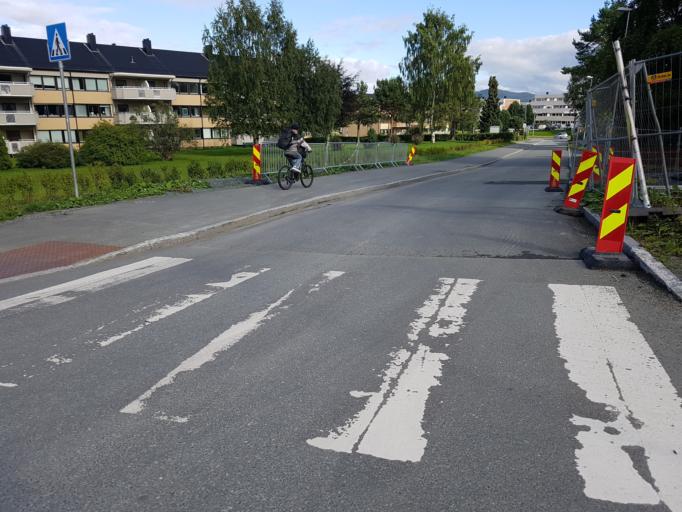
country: NO
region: Sor-Trondelag
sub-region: Trondheim
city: Trondheim
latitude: 63.4285
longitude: 10.4408
